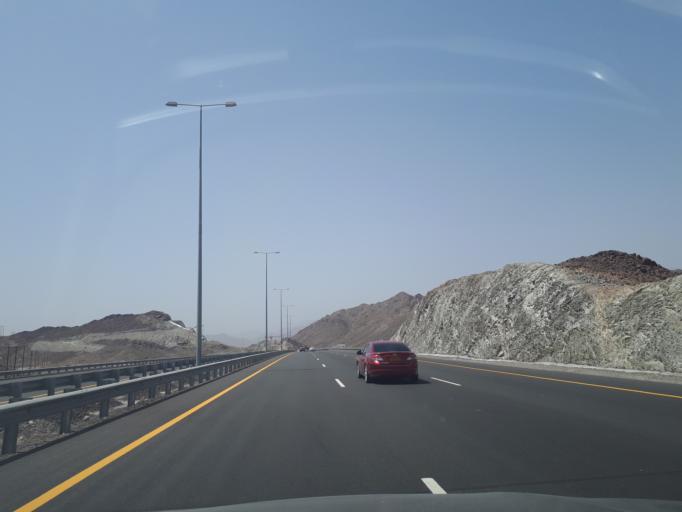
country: OM
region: Muhafazat ad Dakhiliyah
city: Bidbid
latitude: 23.3569
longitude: 58.0914
